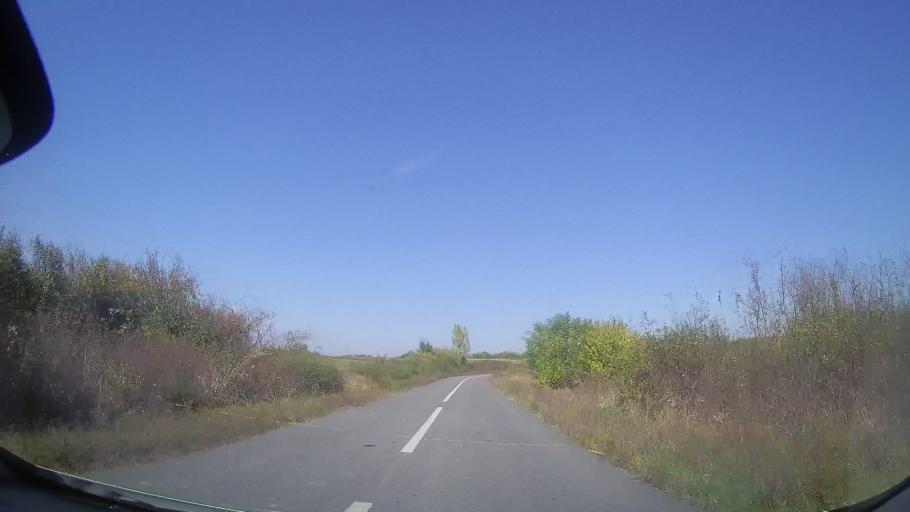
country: RO
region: Timis
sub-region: Comuna Balint
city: Balint
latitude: 45.8228
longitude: 21.8504
